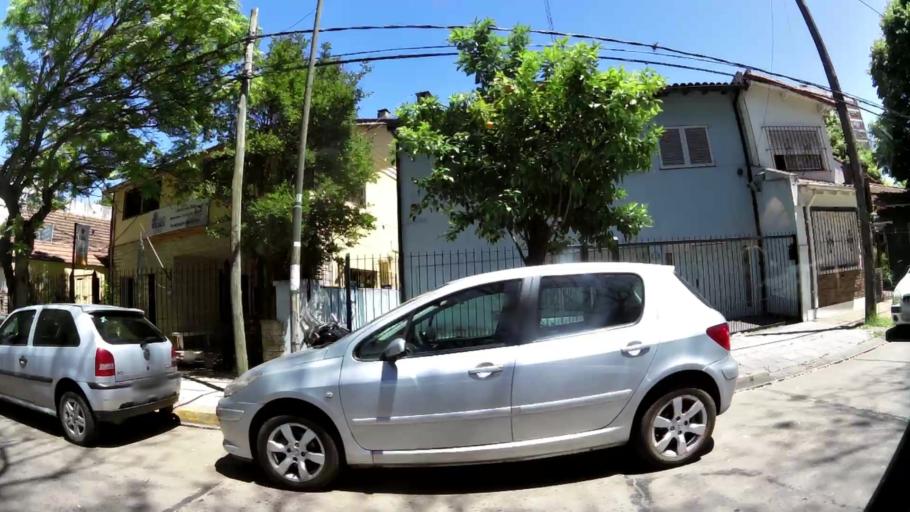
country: AR
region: Buenos Aires
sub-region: Partido de San Isidro
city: San Isidro
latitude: -34.4768
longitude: -58.5085
